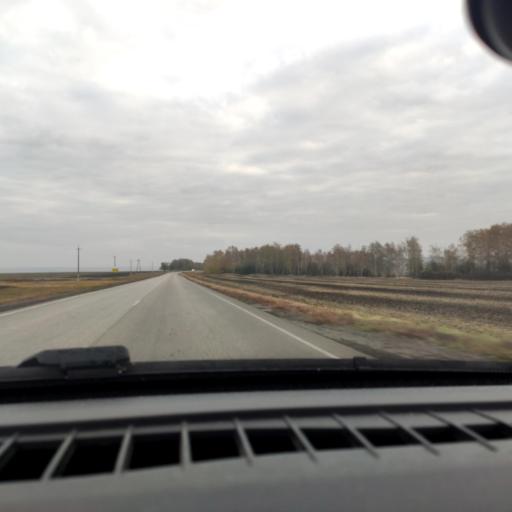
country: RU
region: Belgorod
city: Ilovka
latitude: 50.7544
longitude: 38.7225
